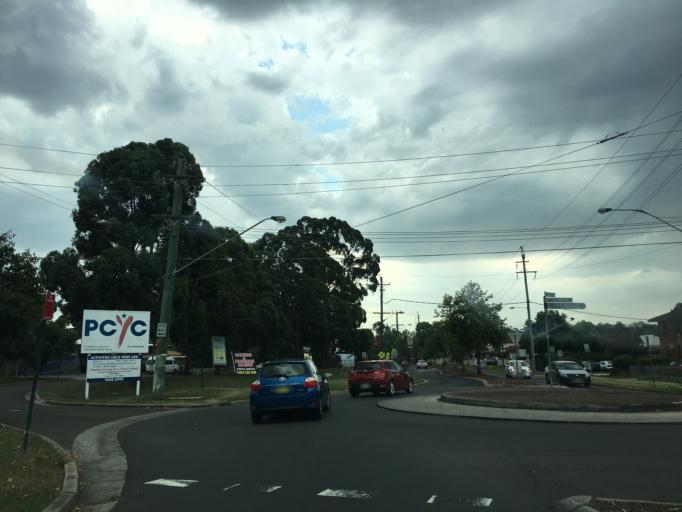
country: AU
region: New South Wales
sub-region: Liverpool
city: Miller
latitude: -33.9214
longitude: 150.8886
